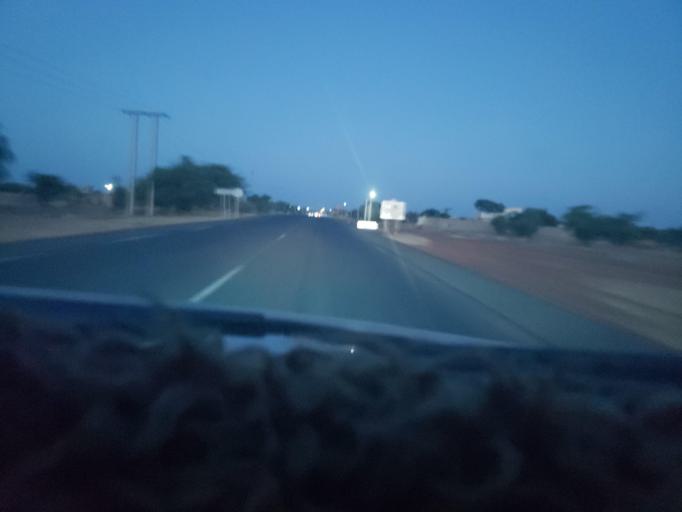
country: SN
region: Louga
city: Ndibene Dahra
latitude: 15.3811
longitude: -15.2453
